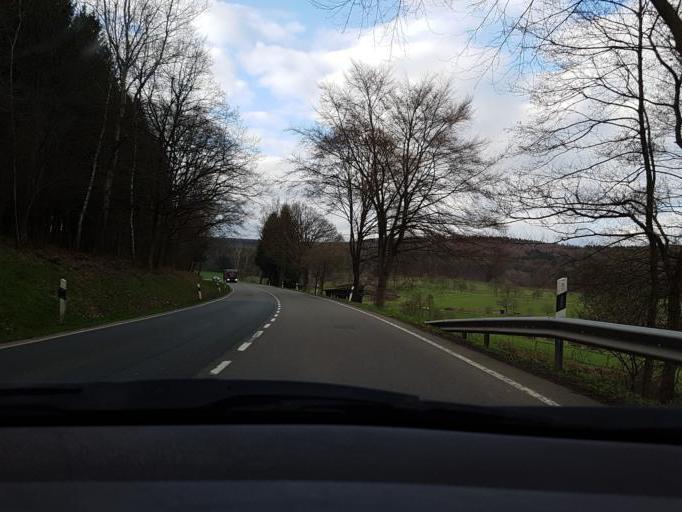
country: DE
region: Lower Saxony
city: Bodenfelde
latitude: 51.7053
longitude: 9.5472
